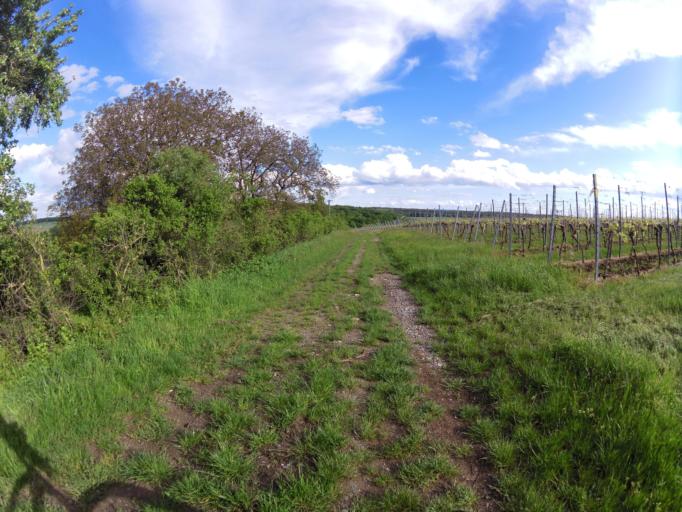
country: DE
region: Bavaria
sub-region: Regierungsbezirk Unterfranken
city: Volkach
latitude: 49.8798
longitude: 10.2664
